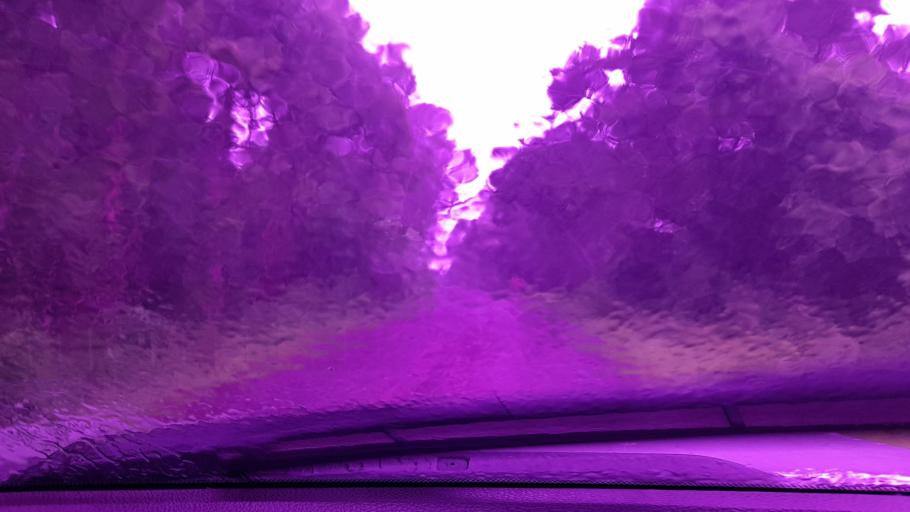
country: ET
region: Oromiya
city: Metu
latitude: 8.4649
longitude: 35.6394
